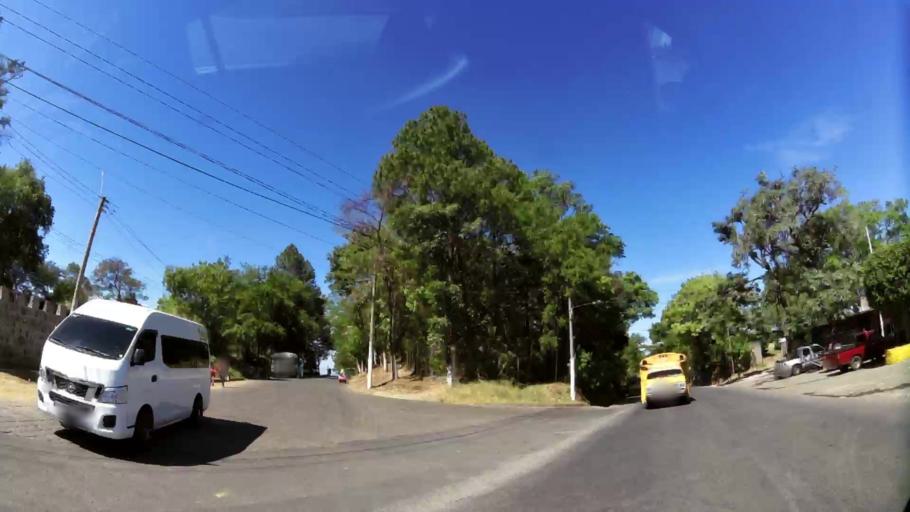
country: SV
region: Ahuachapan
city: Ahuachapan
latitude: 13.9223
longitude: -89.8417
